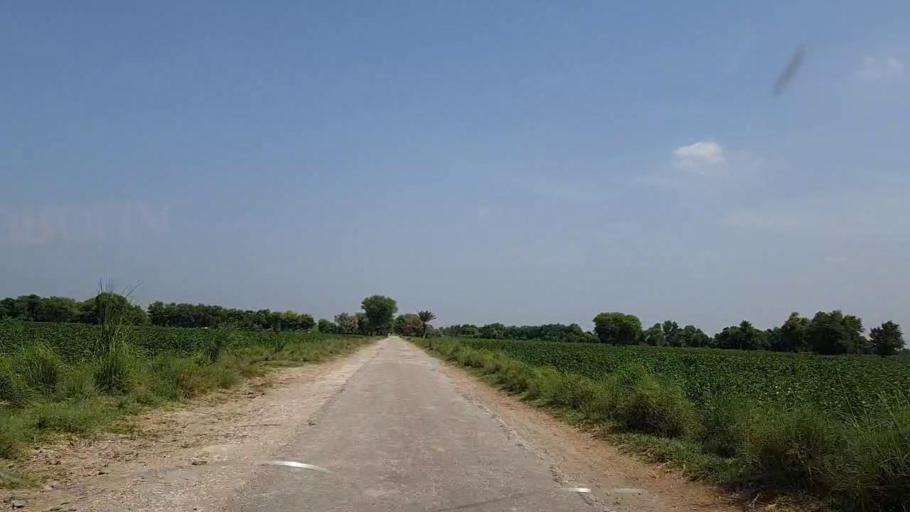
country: PK
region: Sindh
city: Adilpur
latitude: 27.8313
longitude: 69.2906
